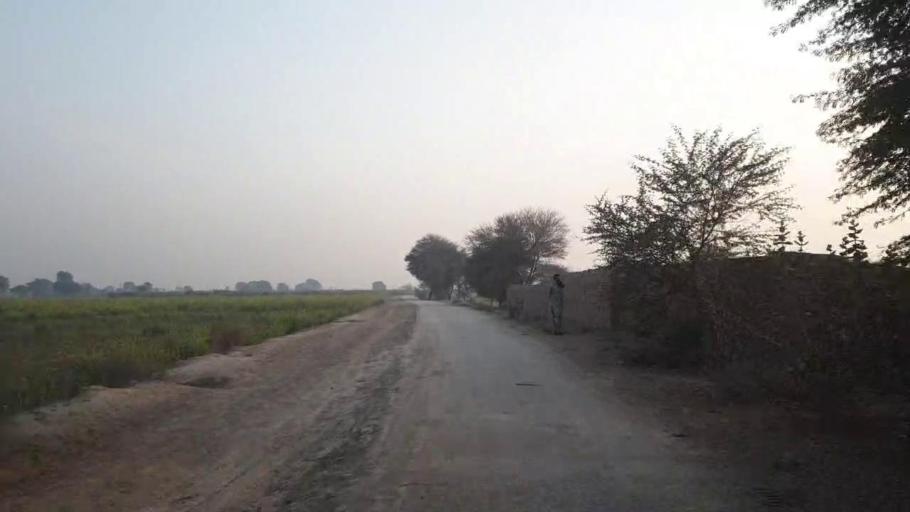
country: PK
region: Sindh
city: Bhit Shah
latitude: 25.7766
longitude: 68.4621
